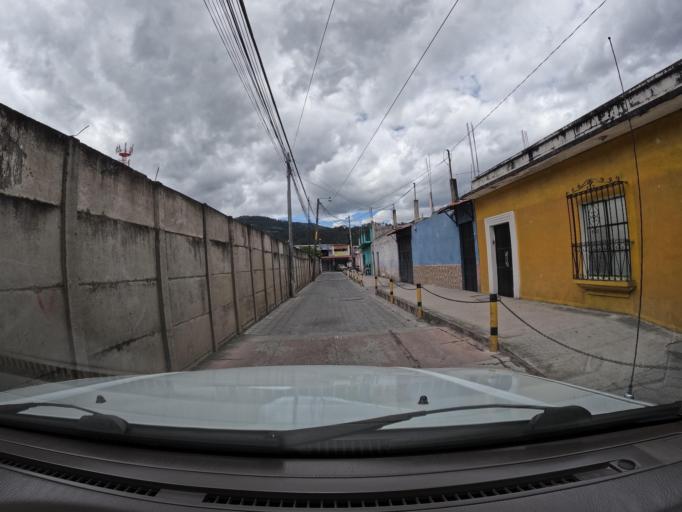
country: GT
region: Sacatepequez
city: Jocotenango
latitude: 14.5779
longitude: -90.7401
